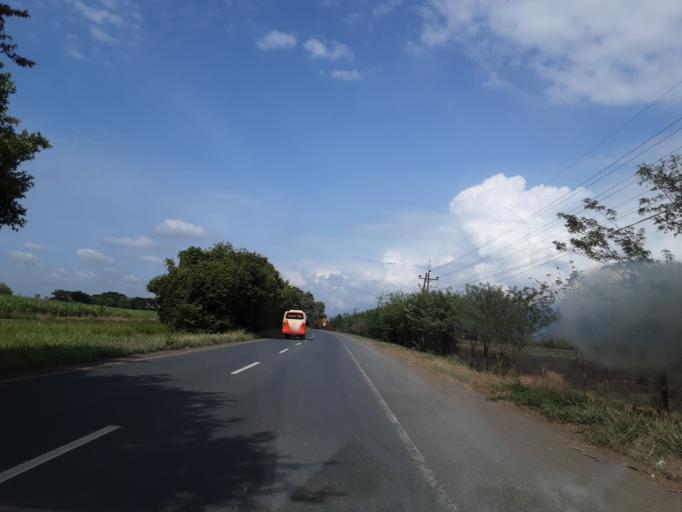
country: CO
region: Valle del Cauca
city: Guacari
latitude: 3.7868
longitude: -76.3199
